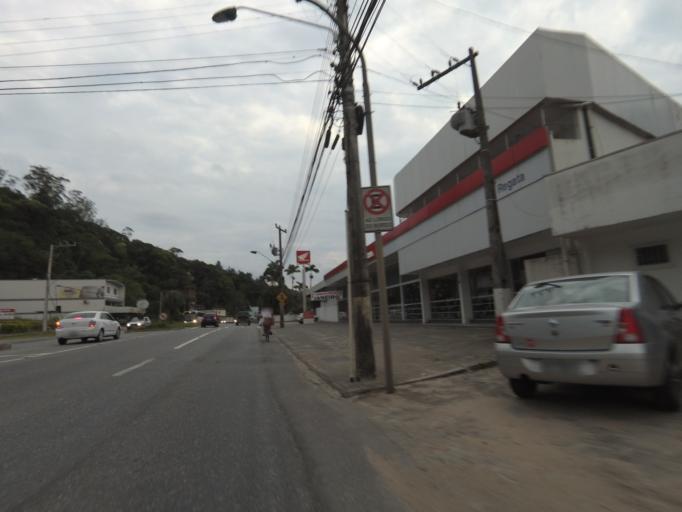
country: BR
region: Santa Catarina
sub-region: Blumenau
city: Blumenau
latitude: -26.9015
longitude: -49.0623
